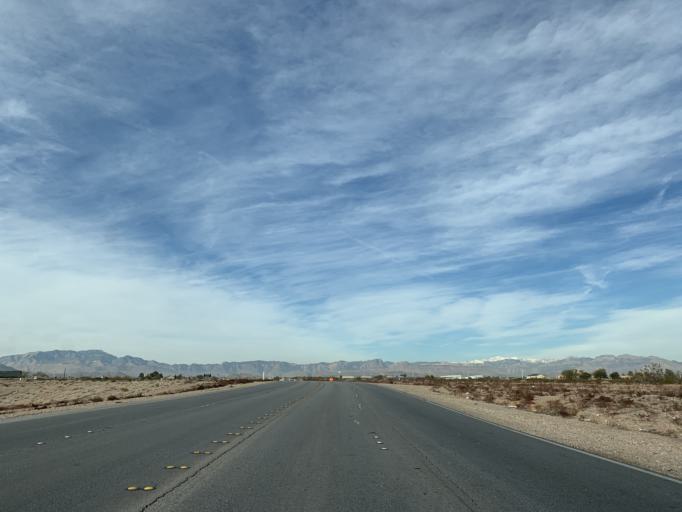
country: US
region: Nevada
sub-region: Clark County
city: Enterprise
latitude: 36.0133
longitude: -115.1865
